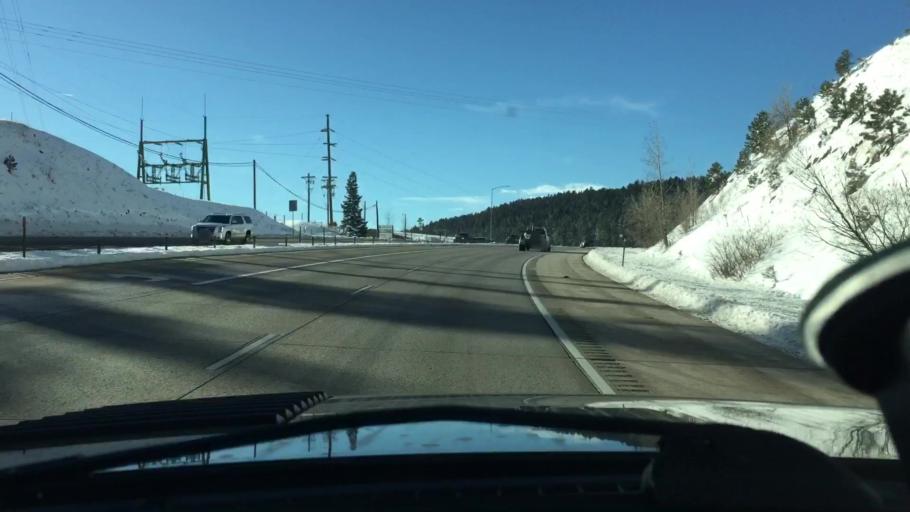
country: US
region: Colorado
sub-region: Jefferson County
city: Indian Hills
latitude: 39.5884
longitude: -105.2209
